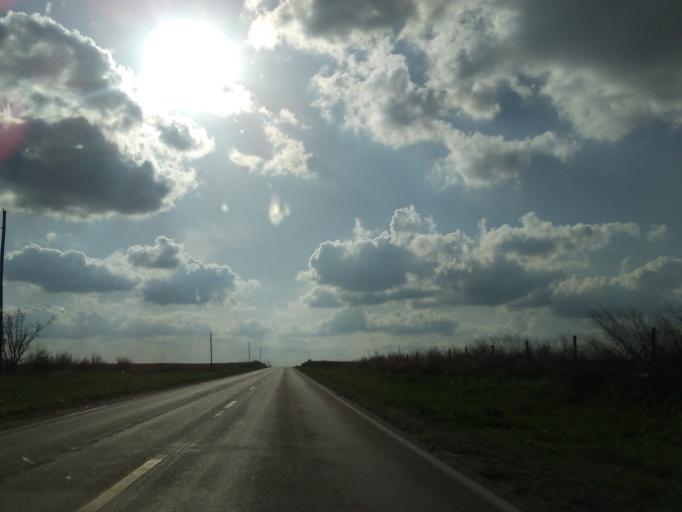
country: US
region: Nebraska
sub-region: Webster County
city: Red Cloud
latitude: 40.0889
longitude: -98.5522
